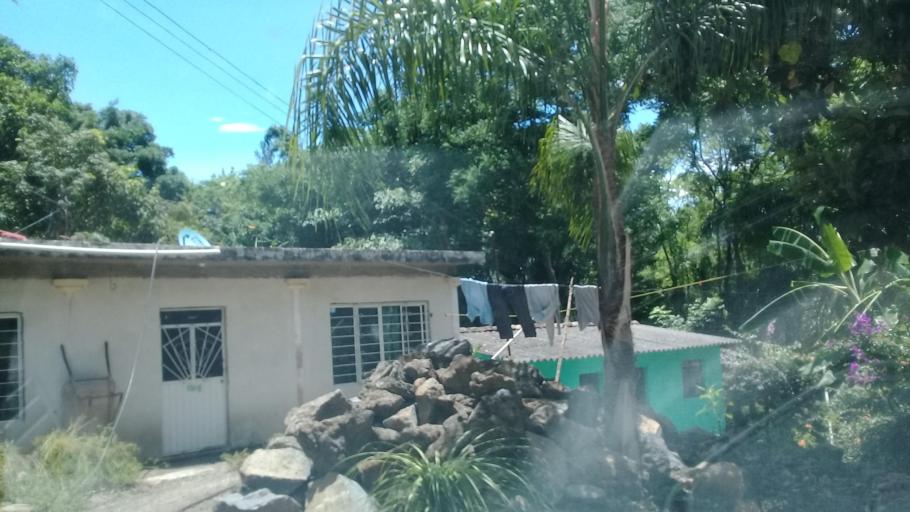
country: MX
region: Veracruz
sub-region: Naolinco
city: El Espinal
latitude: 19.5873
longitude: -96.8729
